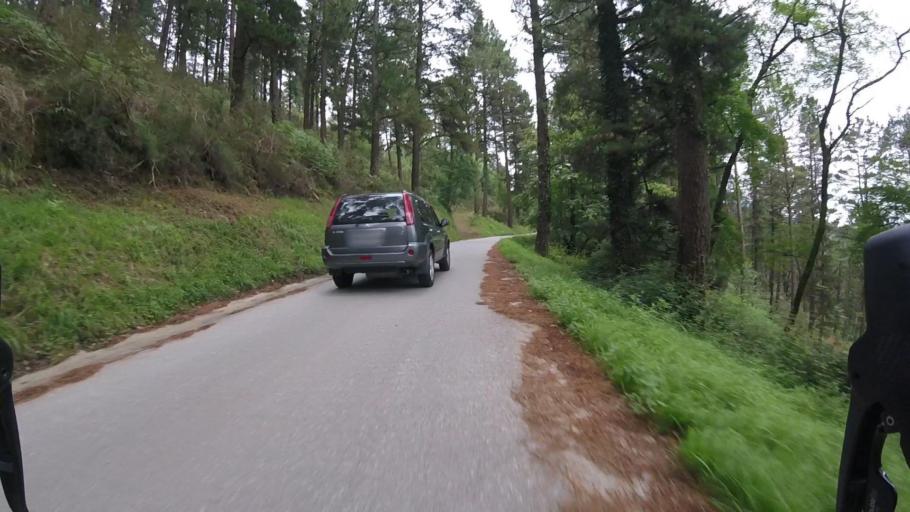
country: ES
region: Basque Country
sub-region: Provincia de Guipuzcoa
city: Errenteria
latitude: 43.2605
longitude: -1.8916
